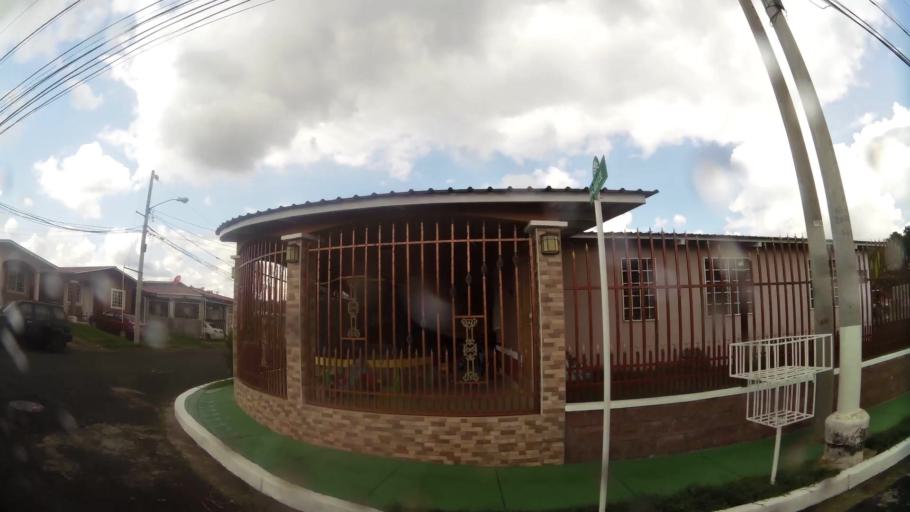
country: PA
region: Panama
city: Nuevo Arraijan
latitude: 8.9409
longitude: -79.7385
